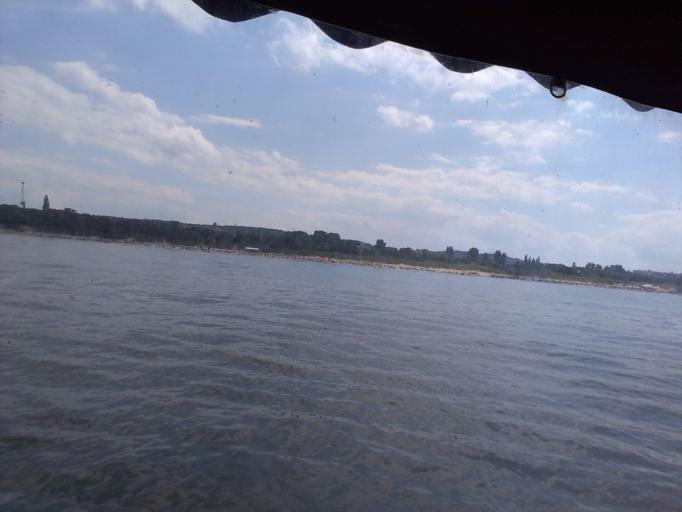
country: PL
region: West Pomeranian Voivodeship
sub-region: Powiat kamienski
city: Miedzyzdroje
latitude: 53.9340
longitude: 14.4389
